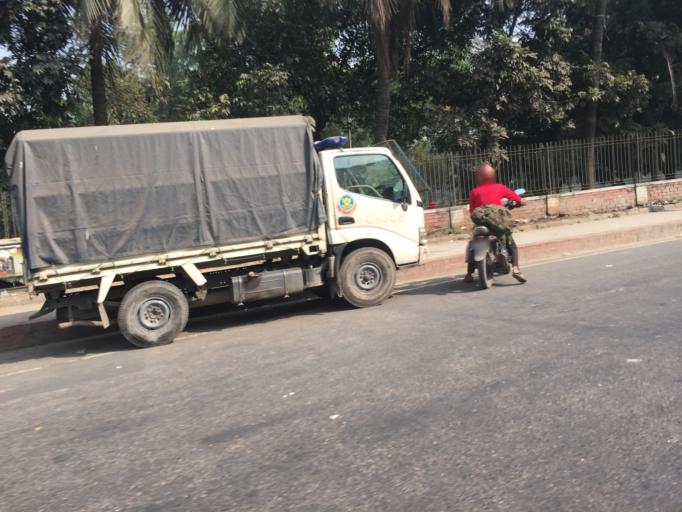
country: BD
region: Dhaka
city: Paltan
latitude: 23.7375
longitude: 90.3992
